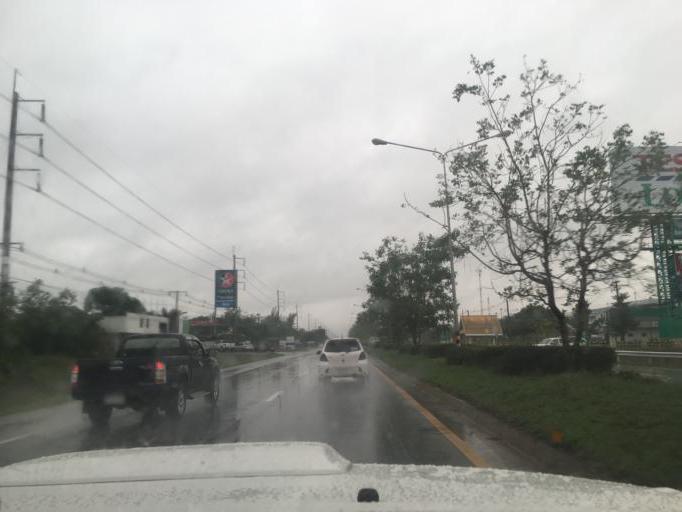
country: TH
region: Changwat Udon Thani
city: Udon Thani
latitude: 17.3809
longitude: 102.7473
